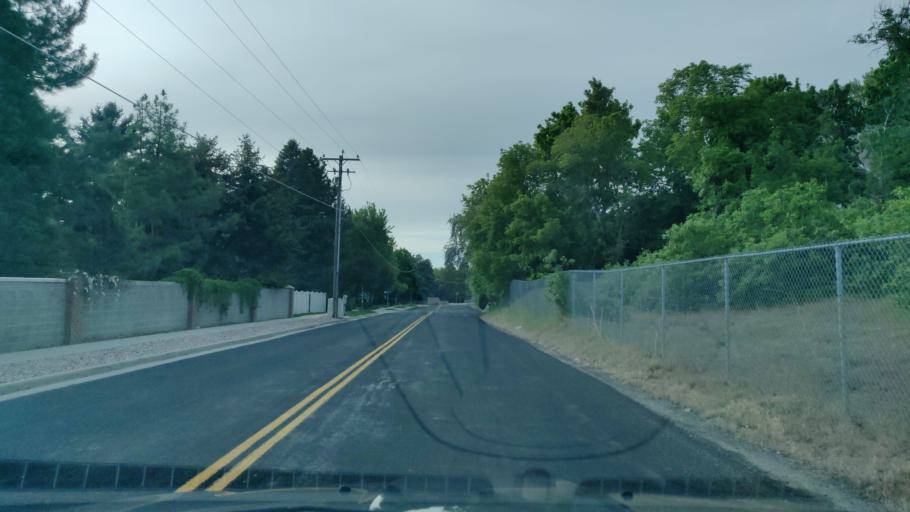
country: US
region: Utah
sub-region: Salt Lake County
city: Cottonwood Heights
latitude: 40.6017
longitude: -111.8037
